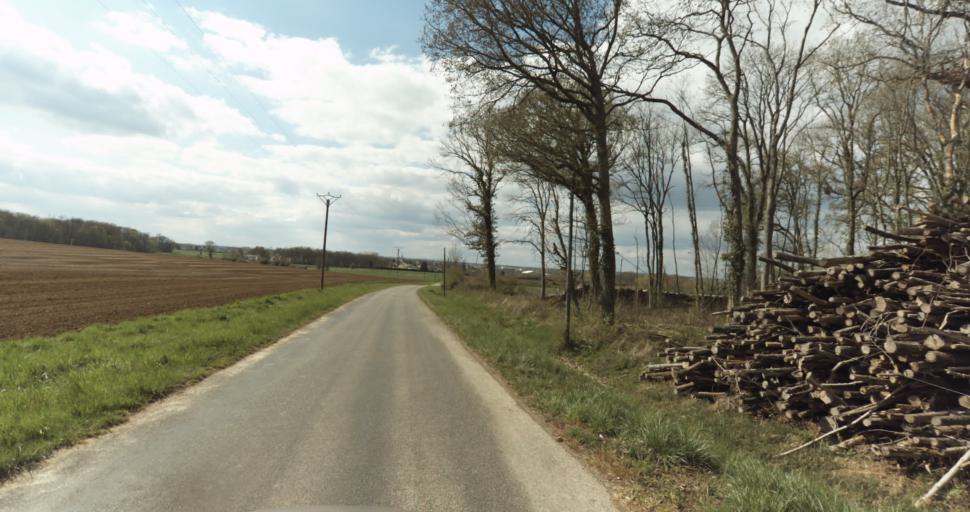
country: FR
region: Bourgogne
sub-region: Departement de la Cote-d'Or
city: Auxonne
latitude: 47.1882
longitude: 5.4240
